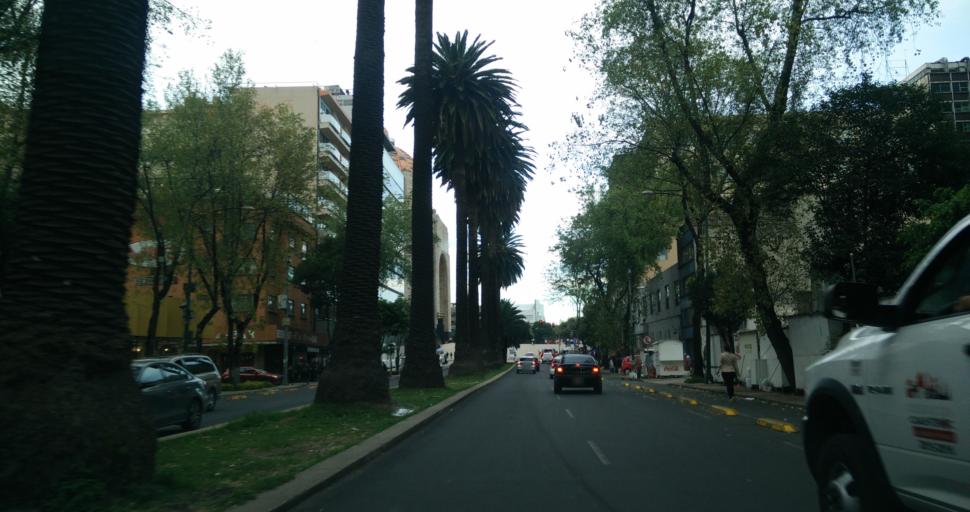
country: MX
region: Mexico City
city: Cuauhtemoc
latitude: 19.4341
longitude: -99.1544
